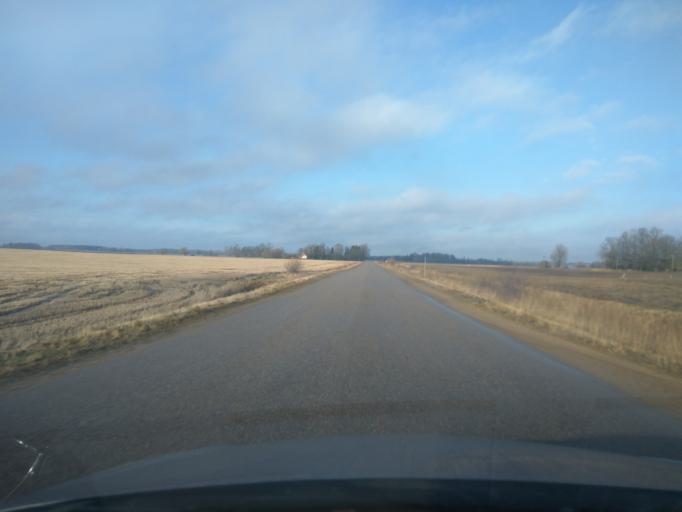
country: LV
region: Saldus Rajons
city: Saldus
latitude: 56.8126
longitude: 22.3807
